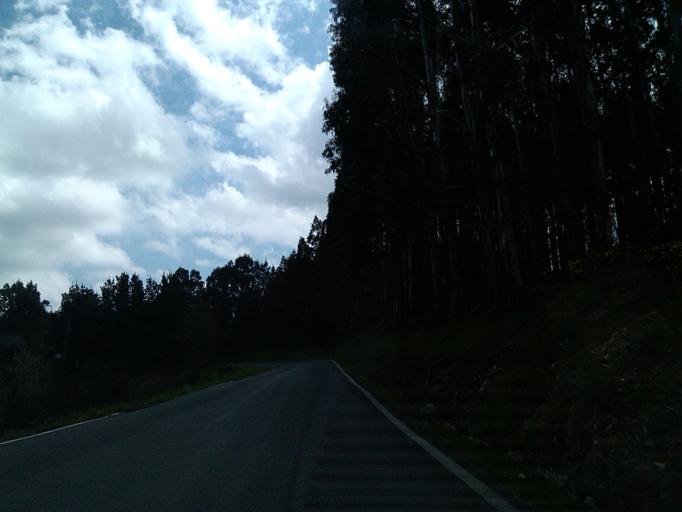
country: ES
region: Galicia
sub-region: Provincia da Coruna
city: Sobrado
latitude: 43.0335
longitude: -7.9370
